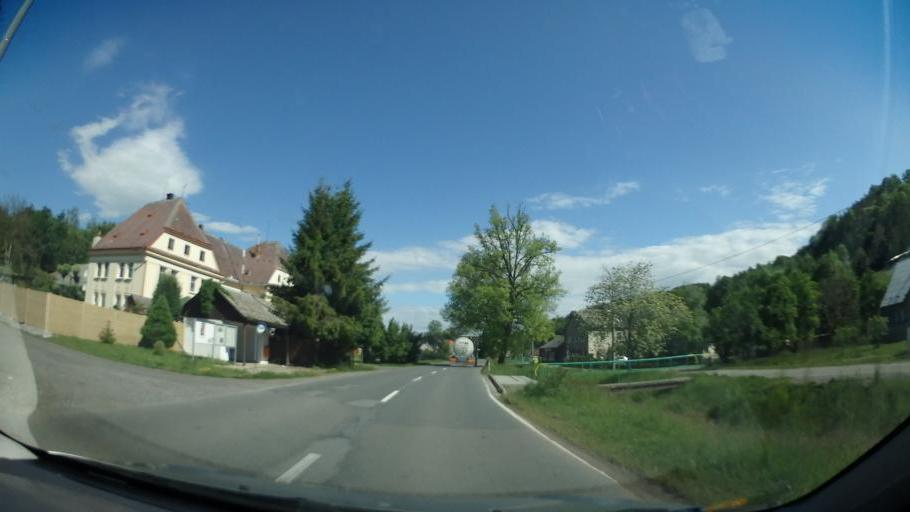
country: CZ
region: Pardubicky
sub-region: Okres Svitavy
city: Moravska Trebova
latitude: 49.7073
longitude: 16.6405
